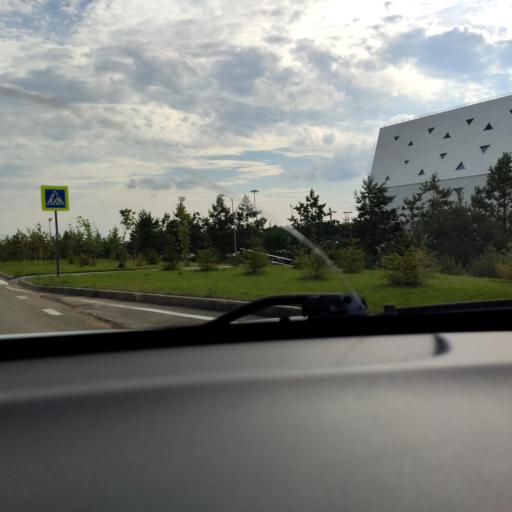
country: RU
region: Tatarstan
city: Sviyazhsk
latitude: 55.7512
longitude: 48.7437
